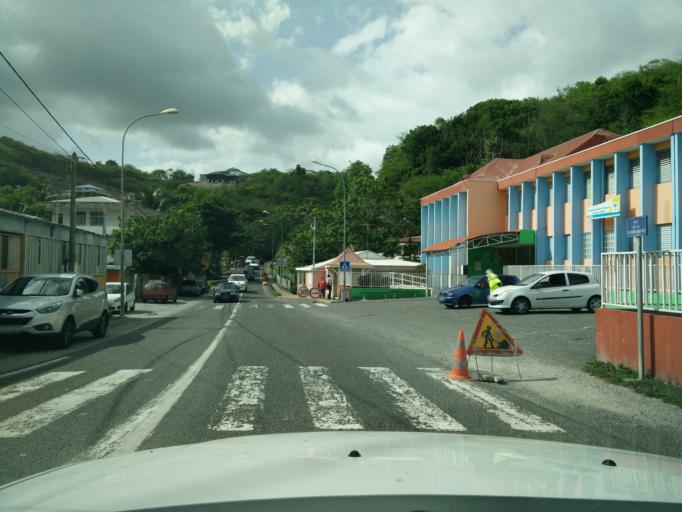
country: GP
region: Guadeloupe
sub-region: Guadeloupe
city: Le Gosier
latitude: 16.2155
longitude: -61.4789
